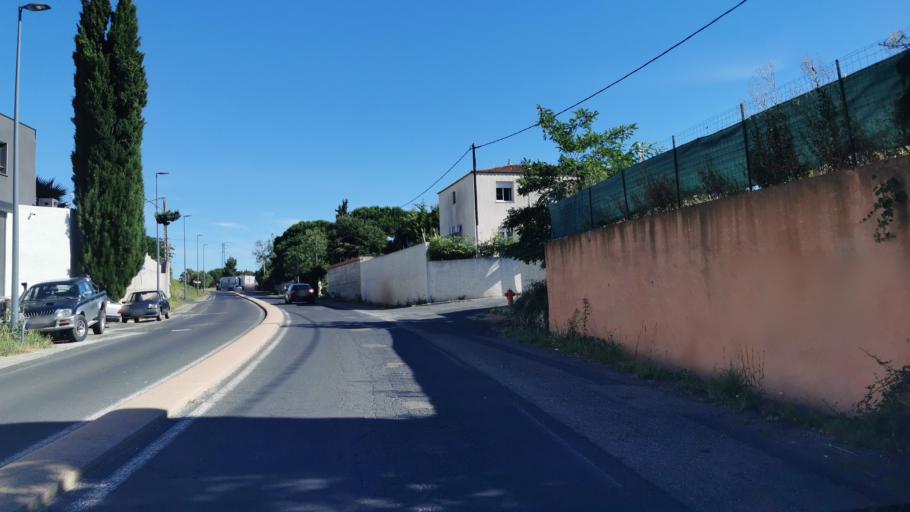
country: FR
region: Languedoc-Roussillon
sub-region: Departement de l'Herault
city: Beziers
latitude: 43.3632
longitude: 3.2119
